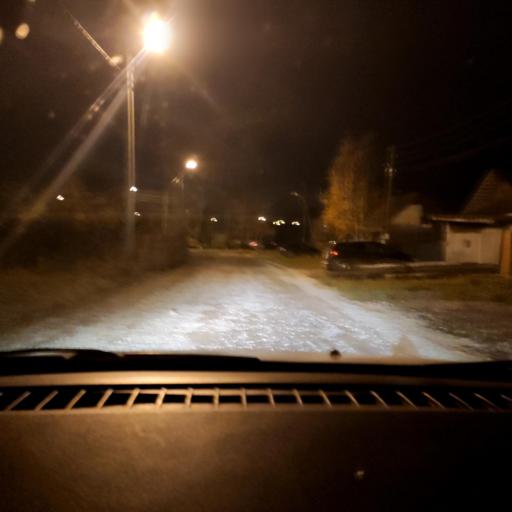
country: RU
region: Perm
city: Perm
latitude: 58.0442
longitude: 56.3613
